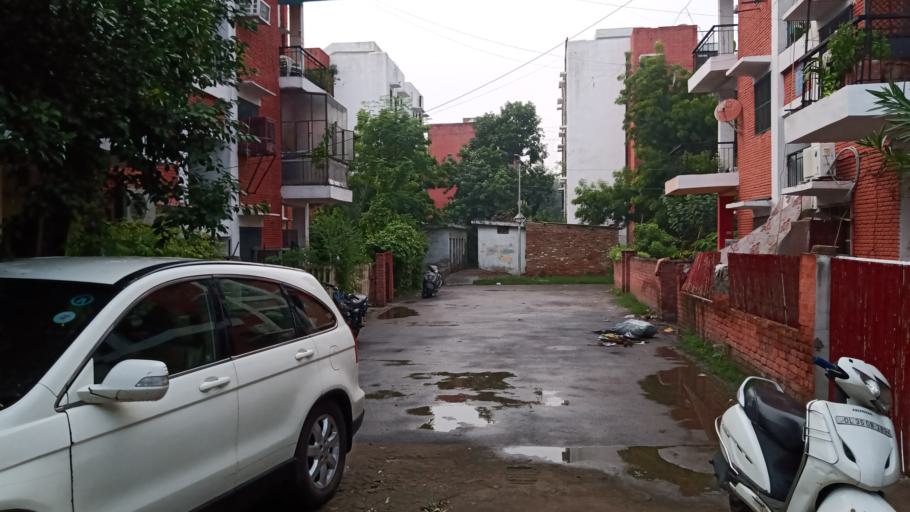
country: IN
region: NCT
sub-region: New Delhi
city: New Delhi
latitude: 28.5739
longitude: 77.2512
